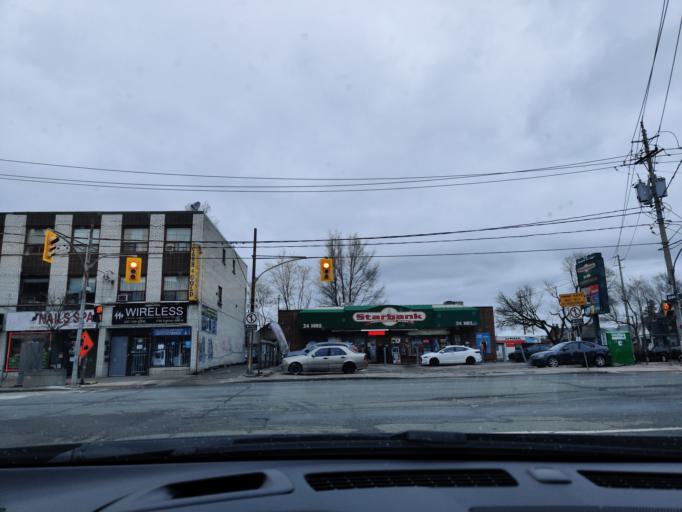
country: CA
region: Ontario
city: Toronto
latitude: 43.6961
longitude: -79.4476
